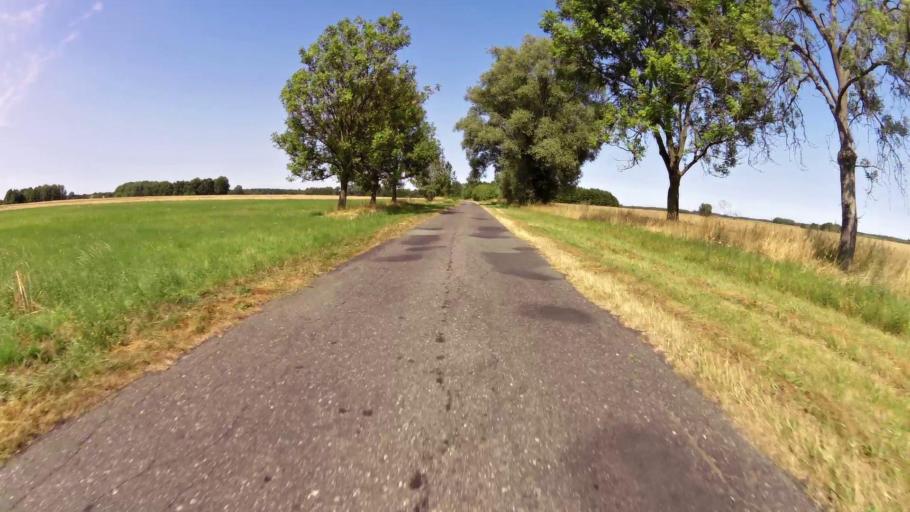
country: PL
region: West Pomeranian Voivodeship
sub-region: Powiat stargardzki
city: Suchan
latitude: 53.2828
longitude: 15.3624
